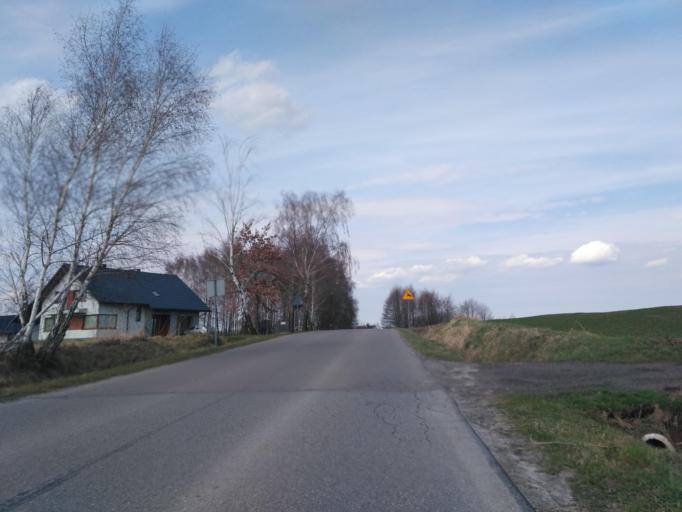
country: PL
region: Subcarpathian Voivodeship
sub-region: Powiat ropczycko-sedziszowski
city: Iwierzyce
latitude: 50.0003
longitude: 21.7972
